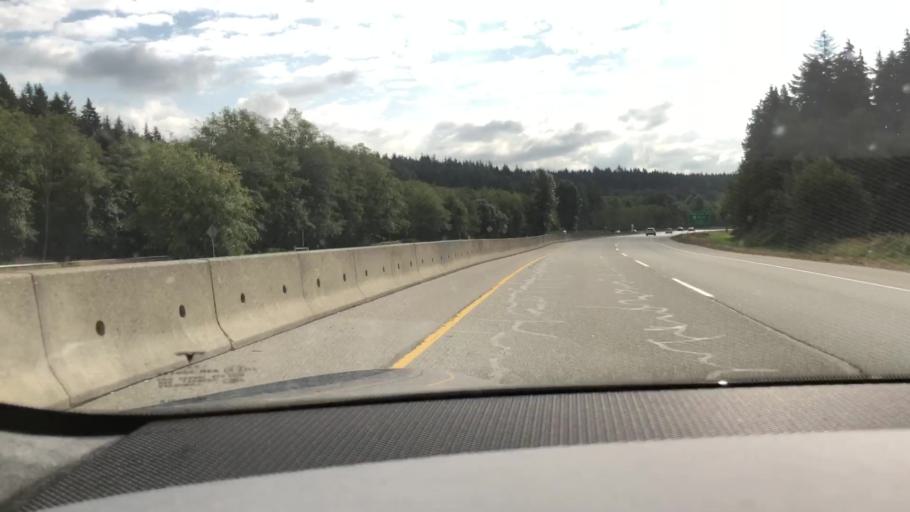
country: CA
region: British Columbia
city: Delta
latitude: 49.1141
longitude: -122.9142
